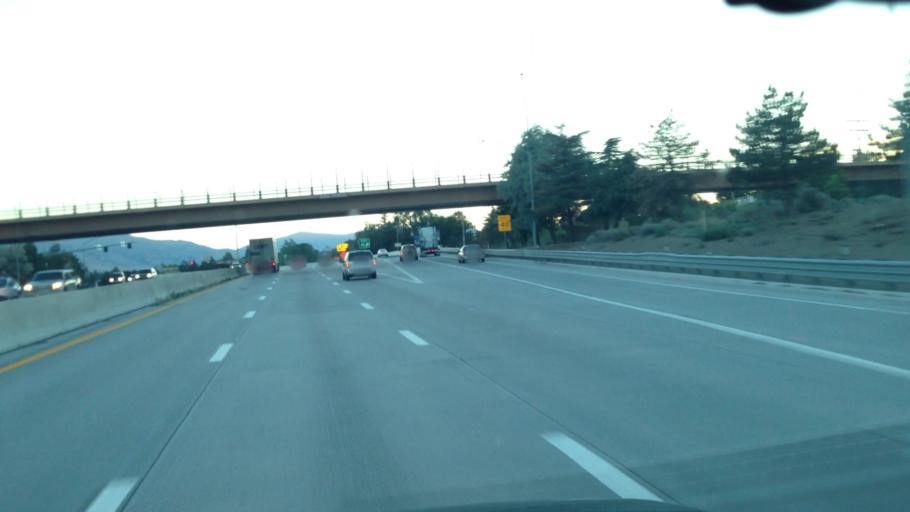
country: US
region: Nevada
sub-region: Washoe County
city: Reno
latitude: 39.5316
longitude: -119.8254
